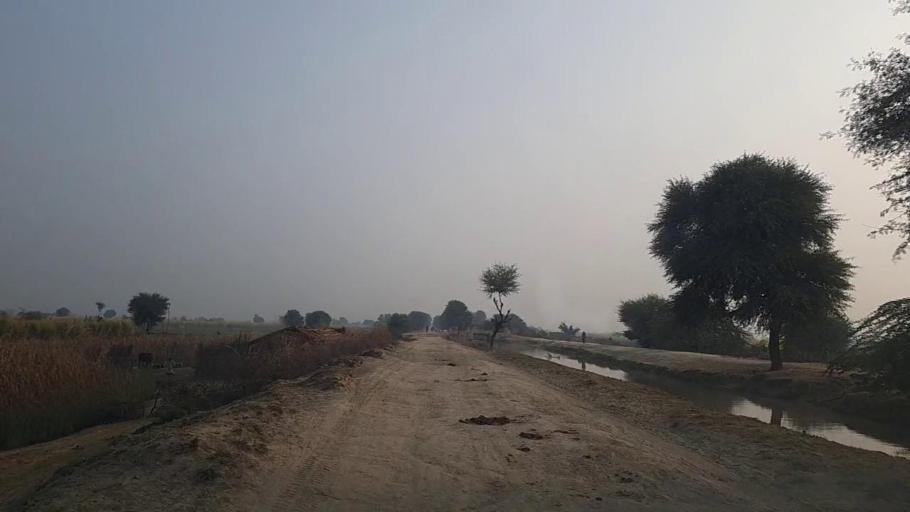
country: PK
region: Sindh
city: Khadro
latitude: 26.1226
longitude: 68.8015
